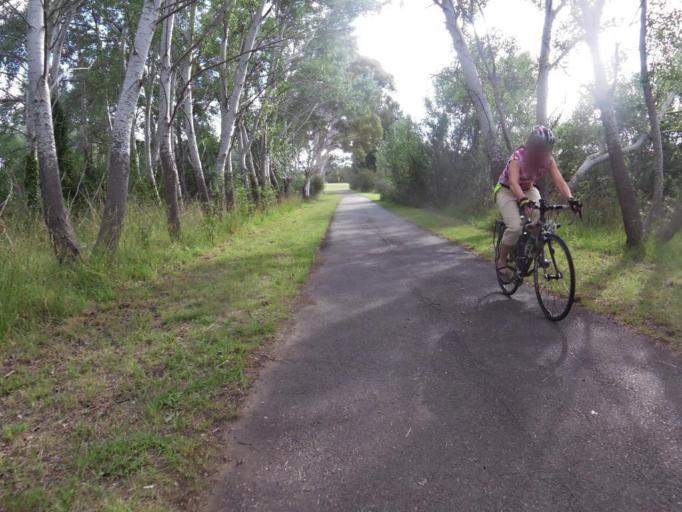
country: AU
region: Australian Capital Territory
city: Belconnen
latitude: -35.2182
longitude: 149.0822
